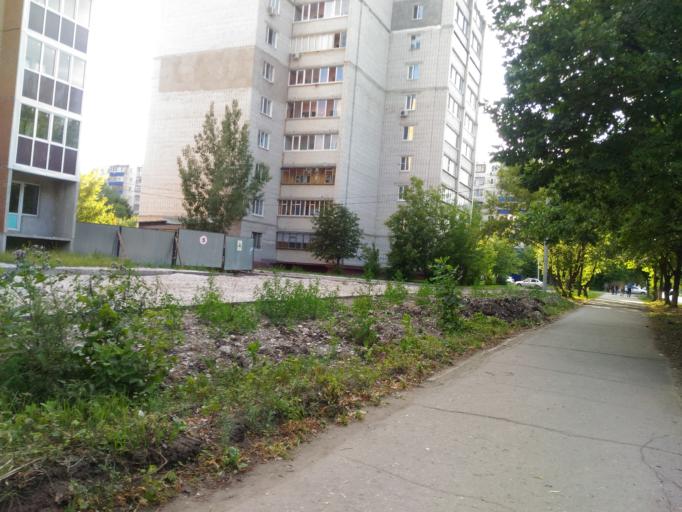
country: RU
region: Ulyanovsk
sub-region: Ulyanovskiy Rayon
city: Ulyanovsk
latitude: 54.2822
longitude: 48.2919
